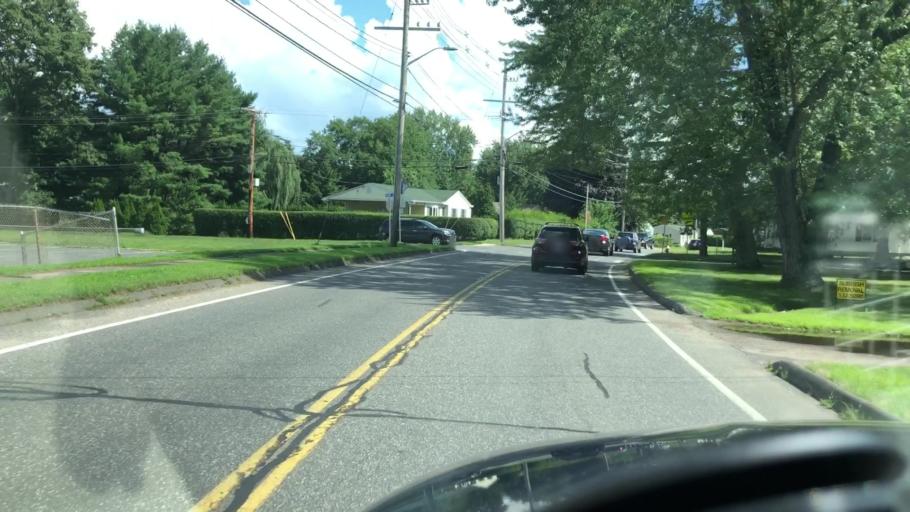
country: US
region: Massachusetts
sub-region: Hampden County
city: Holyoke
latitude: 42.1838
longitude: -72.6491
